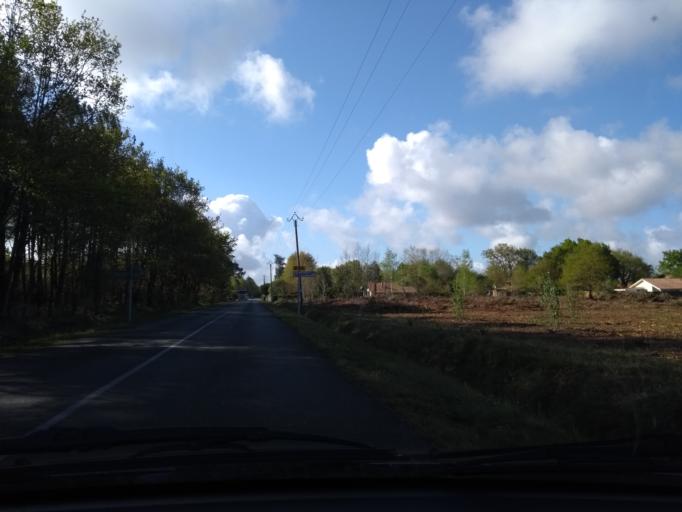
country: FR
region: Aquitaine
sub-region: Departement des Landes
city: Sanguinet
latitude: 44.4725
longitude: -1.0701
